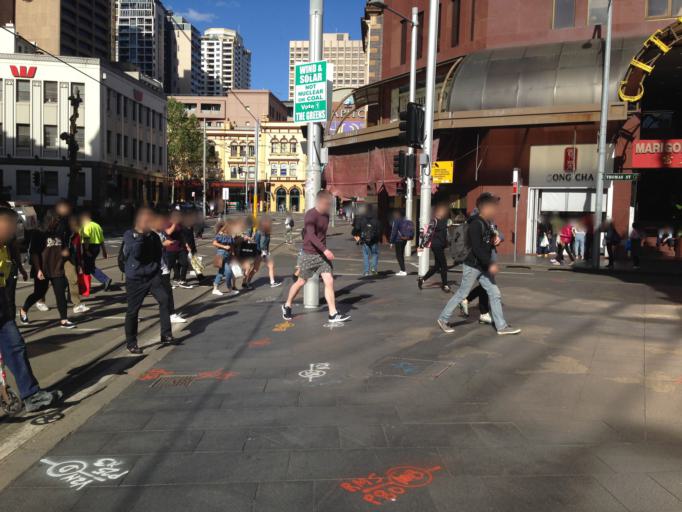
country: AU
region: New South Wales
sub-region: City of Sydney
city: Haymarket
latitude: -33.8795
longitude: 151.2044
